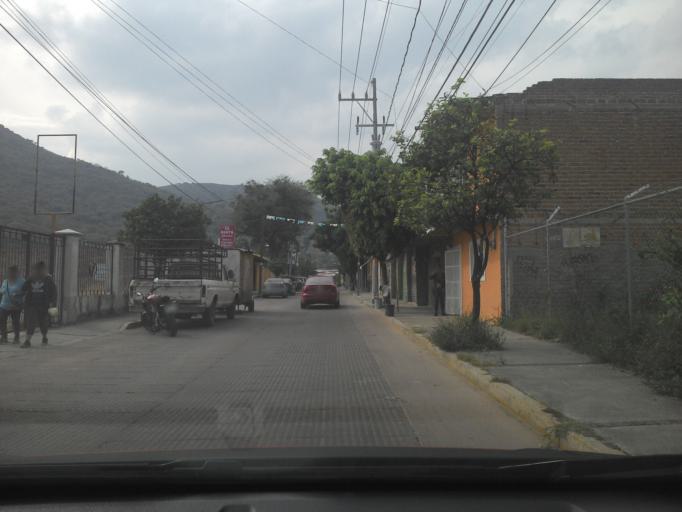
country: MX
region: Jalisco
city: Tlajomulco de Zuniga
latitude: 20.4776
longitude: -103.4508
